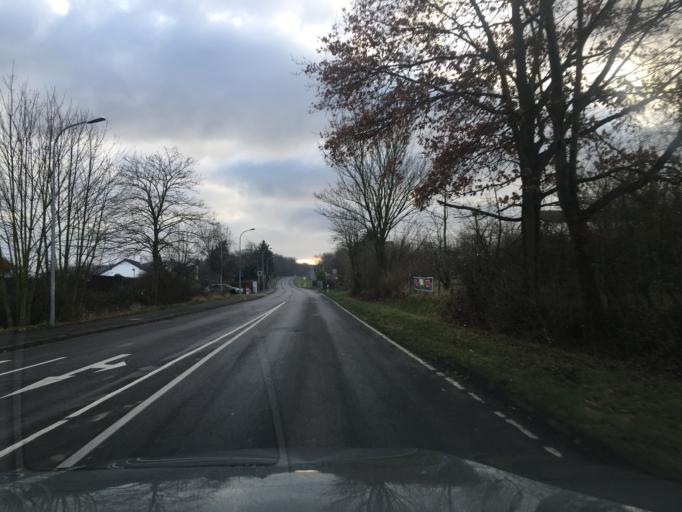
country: DE
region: North Rhine-Westphalia
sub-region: Regierungsbezirk Koln
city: Wachtberg
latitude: 50.6210
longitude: 7.1260
